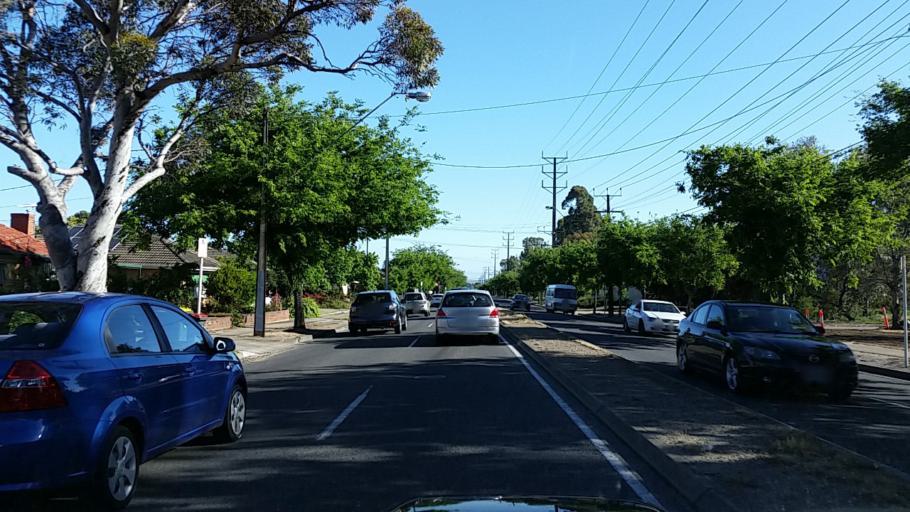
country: AU
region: South Australia
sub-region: Charles Sturt
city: Allenby Gardens
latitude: -34.9145
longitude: 138.5482
